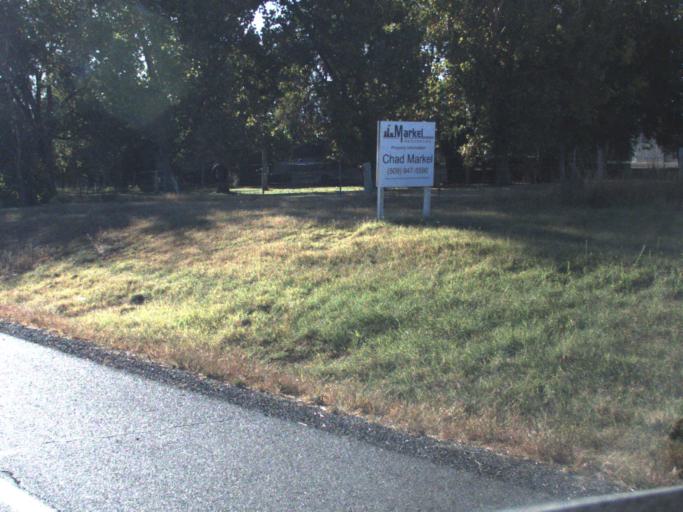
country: US
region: Washington
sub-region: Benton County
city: West Richland
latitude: 46.2978
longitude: -119.3268
